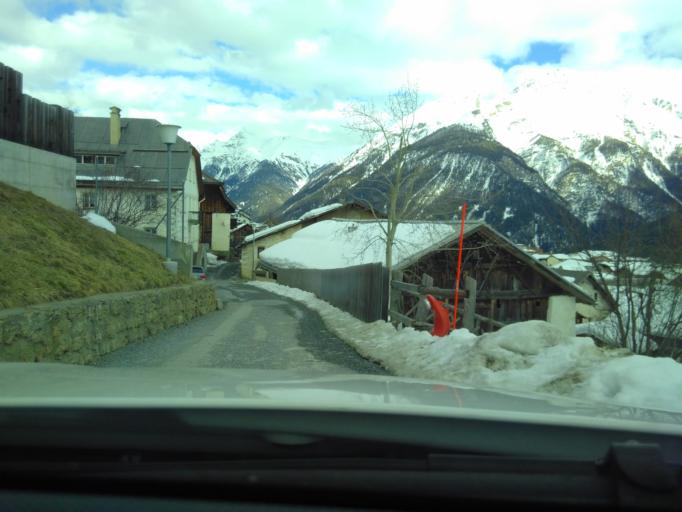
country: CH
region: Grisons
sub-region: Inn District
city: Scuol
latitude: 46.8172
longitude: 10.3340
